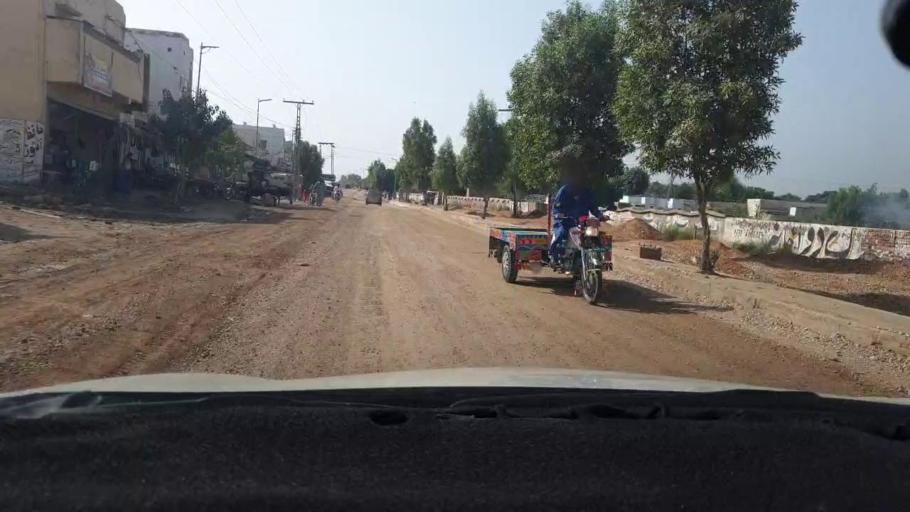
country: PK
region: Sindh
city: Sanghar
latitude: 26.0404
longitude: 68.9502
